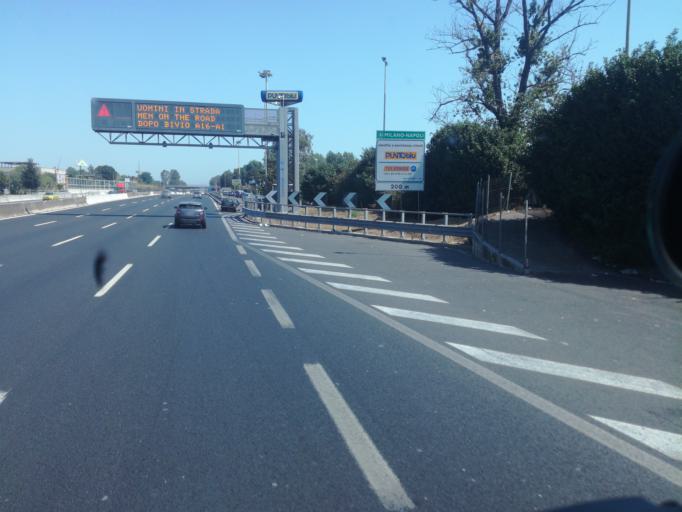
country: IT
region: Campania
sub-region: Provincia di Napoli
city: Arpino
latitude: 40.9004
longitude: 14.3193
